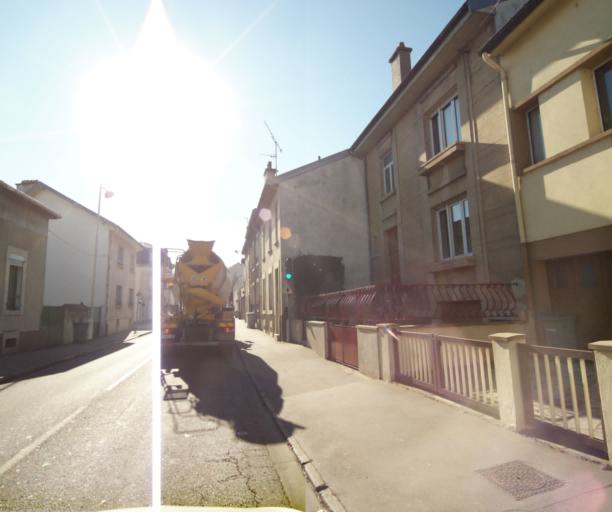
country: FR
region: Lorraine
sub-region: Departement de Meurthe-et-Moselle
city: Maxeville
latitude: 48.7061
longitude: 6.1732
